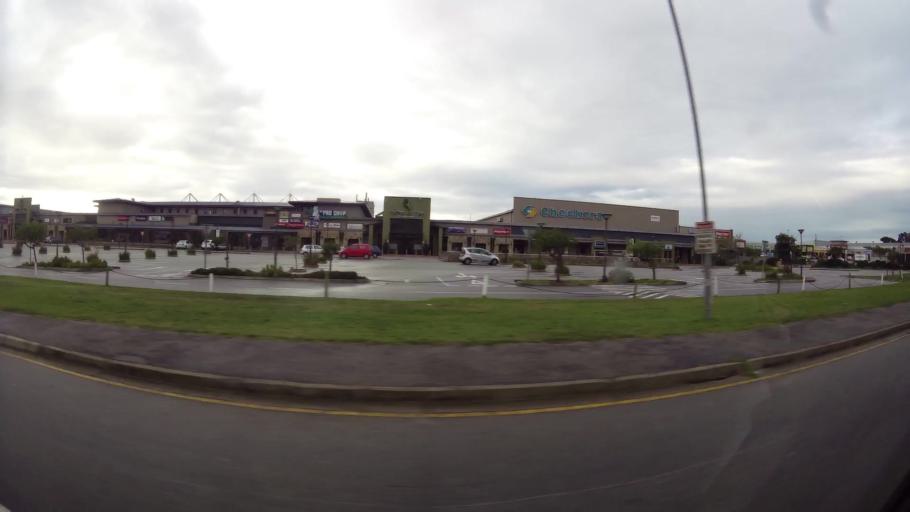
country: ZA
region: Eastern Cape
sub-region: Nelson Mandela Bay Metropolitan Municipality
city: Port Elizabeth
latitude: -33.9833
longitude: 25.5533
